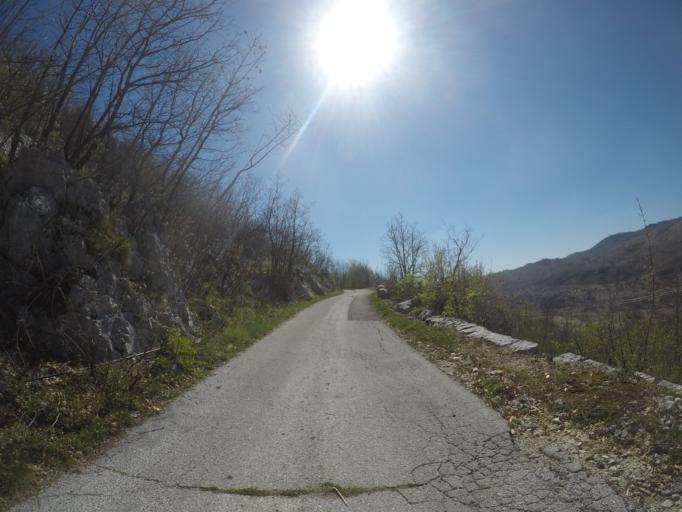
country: ME
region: Cetinje
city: Cetinje
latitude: 42.5282
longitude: 18.9509
